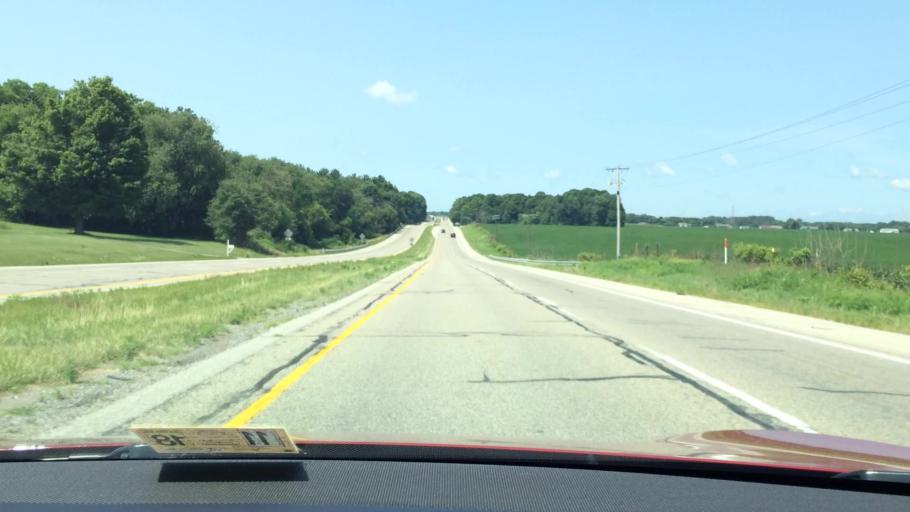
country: US
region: Indiana
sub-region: LaPorte County
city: Hudson Lake
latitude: 41.6728
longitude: -86.5669
